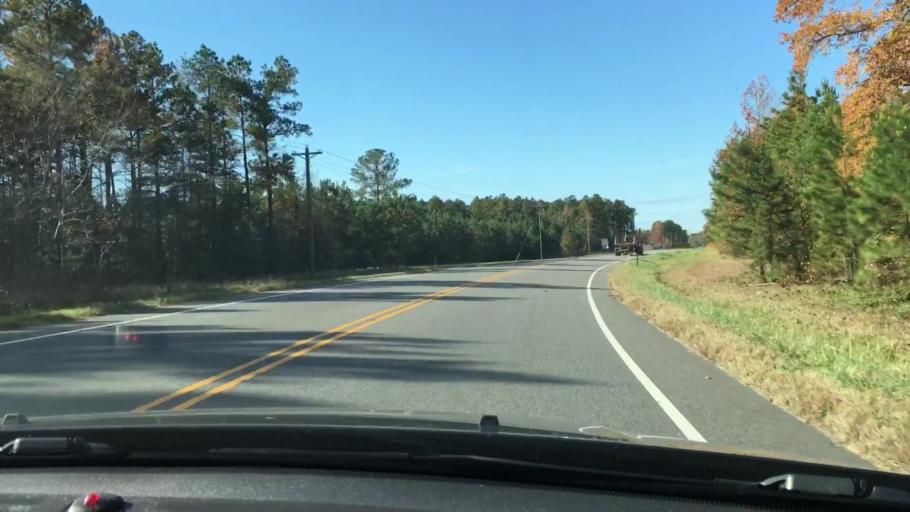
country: US
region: Virginia
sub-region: Hanover County
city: Hanover
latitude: 37.8152
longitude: -77.3128
